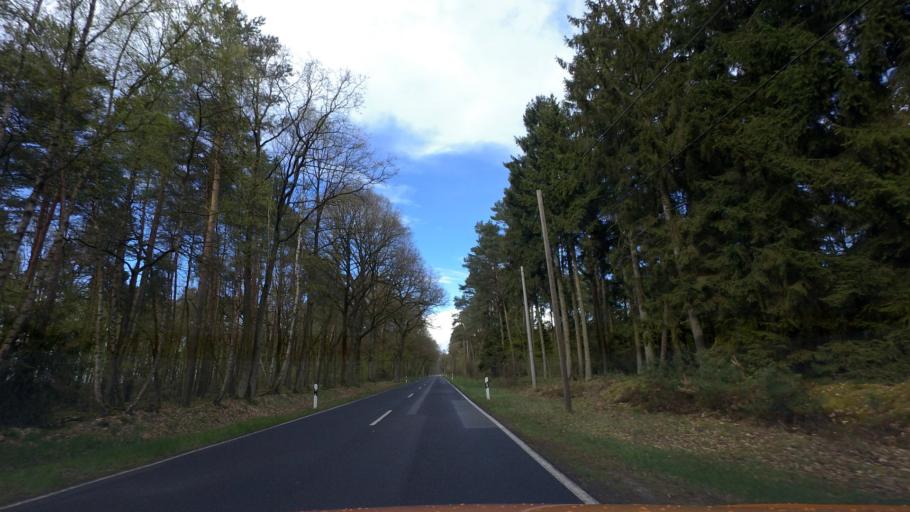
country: DE
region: Mecklenburg-Vorpommern
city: Nostorf
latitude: 53.4188
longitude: 10.6833
